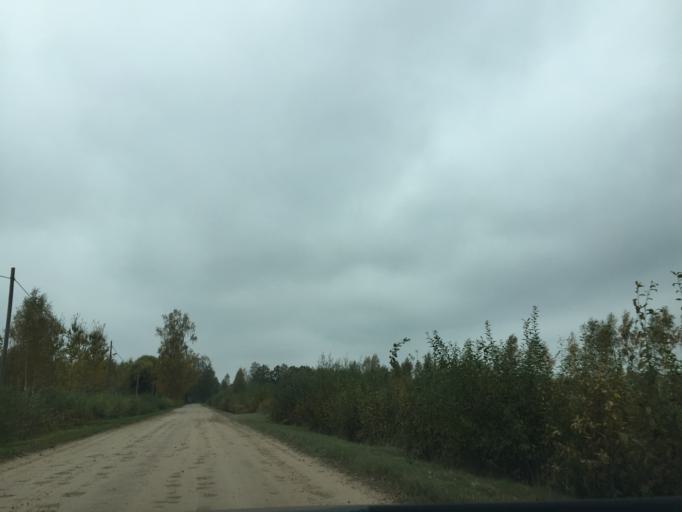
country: LV
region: Ozolnieku
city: Ozolnieki
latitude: 56.6858
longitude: 23.7439
